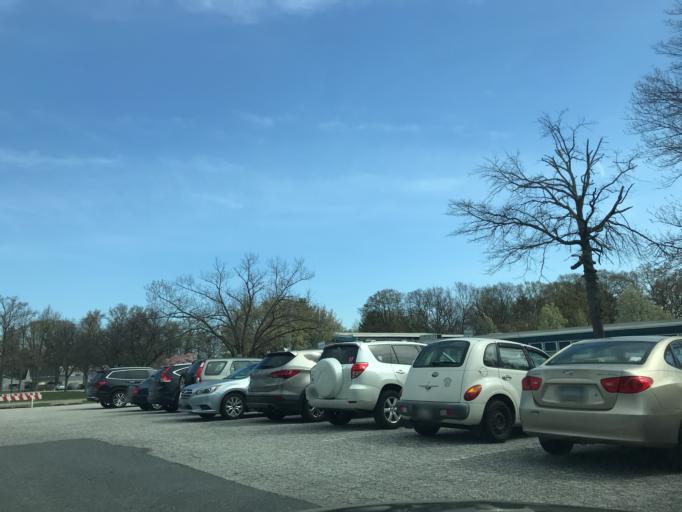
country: US
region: Maryland
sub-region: Baltimore County
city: Middle River
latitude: 39.3046
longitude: -76.4355
